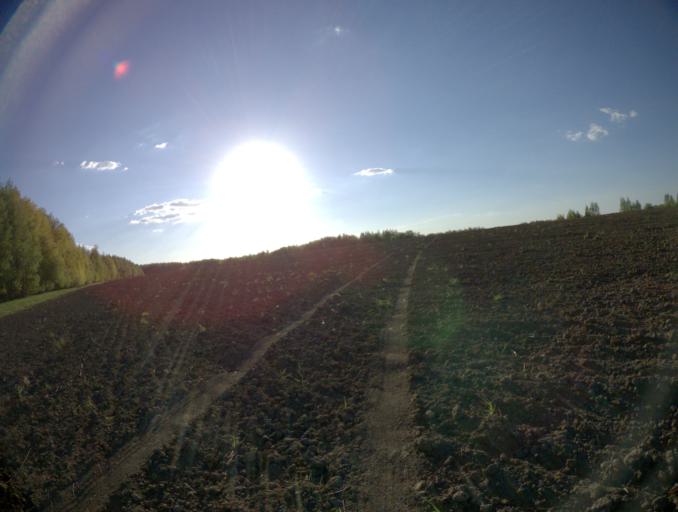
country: RU
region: Ivanovo
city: Gavrilov Posad
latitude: 56.3896
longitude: 40.1186
